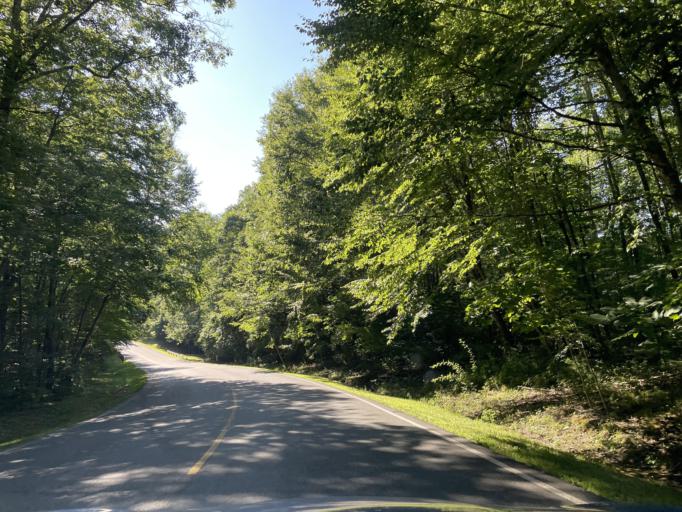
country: US
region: Massachusetts
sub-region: Worcester County
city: Sturbridge
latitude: 42.1465
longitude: -72.0499
